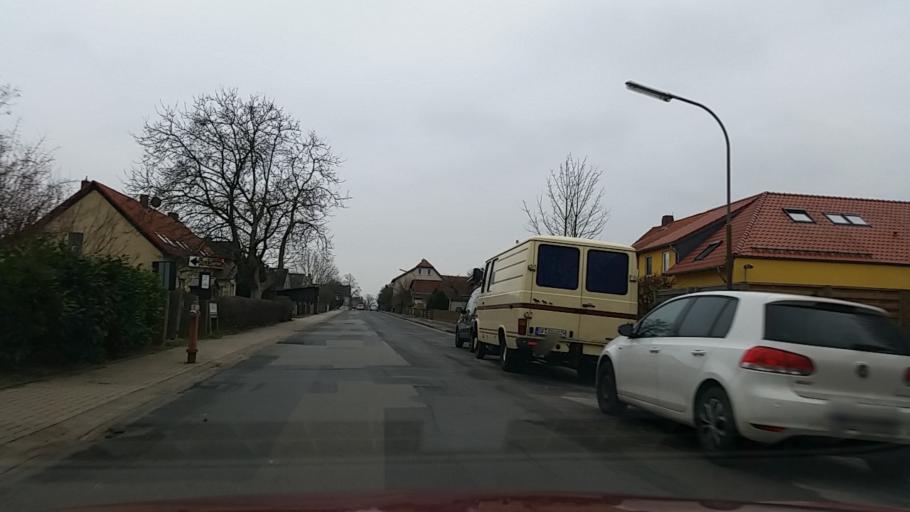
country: DE
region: Lower Saxony
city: Meine
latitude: 52.3573
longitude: 10.5876
